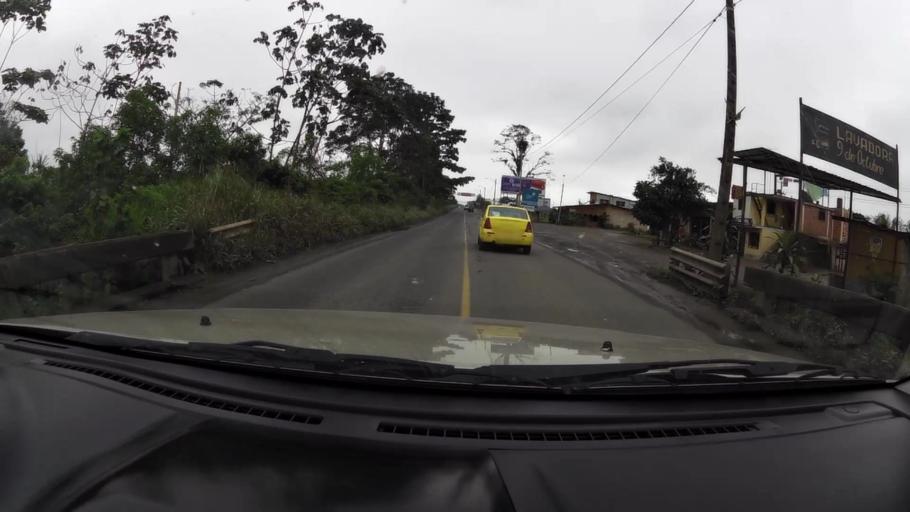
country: EC
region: Guayas
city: Balao
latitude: -3.0739
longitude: -79.7529
